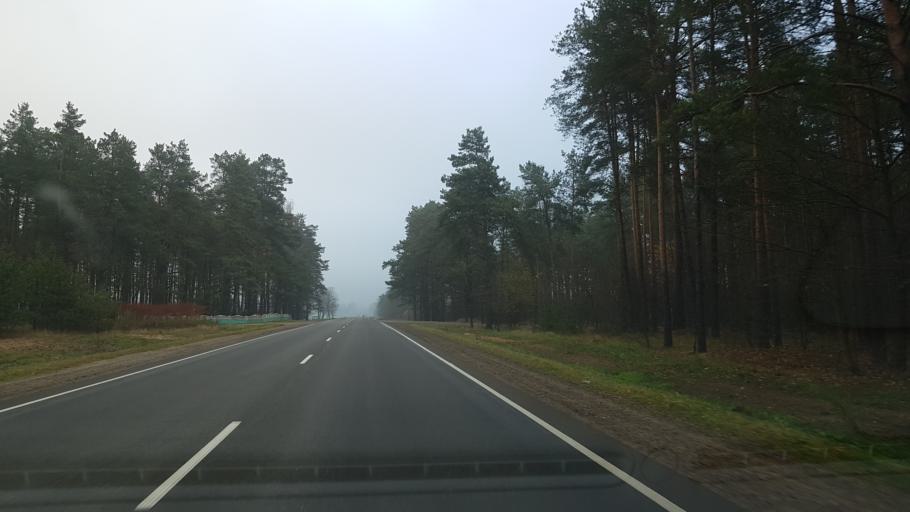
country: BY
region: Mogilev
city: Babruysk
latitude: 53.1661
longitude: 29.3302
